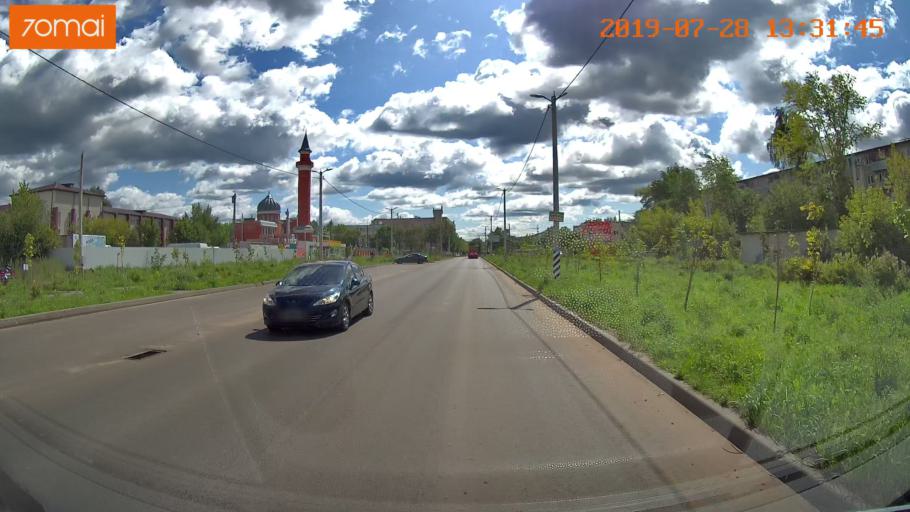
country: RU
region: Ivanovo
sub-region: Gorod Ivanovo
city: Ivanovo
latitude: 56.9657
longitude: 40.9844
